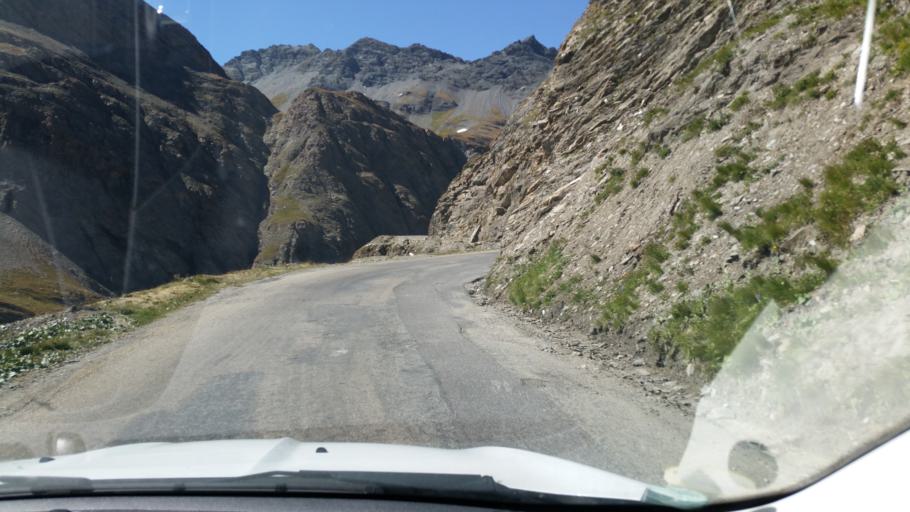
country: FR
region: Rhone-Alpes
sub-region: Departement de la Savoie
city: Val-d'Isere
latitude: 45.4011
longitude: 7.0386
